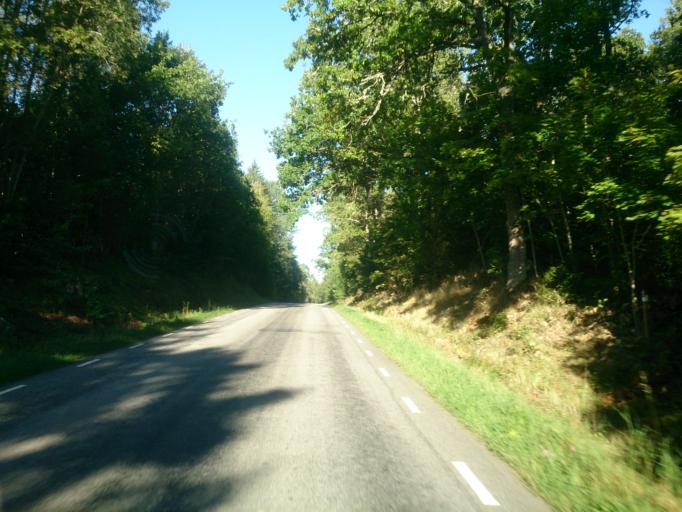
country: SE
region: OEstergoetland
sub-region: Atvidabergs Kommun
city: Atvidaberg
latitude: 58.1818
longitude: 16.0321
